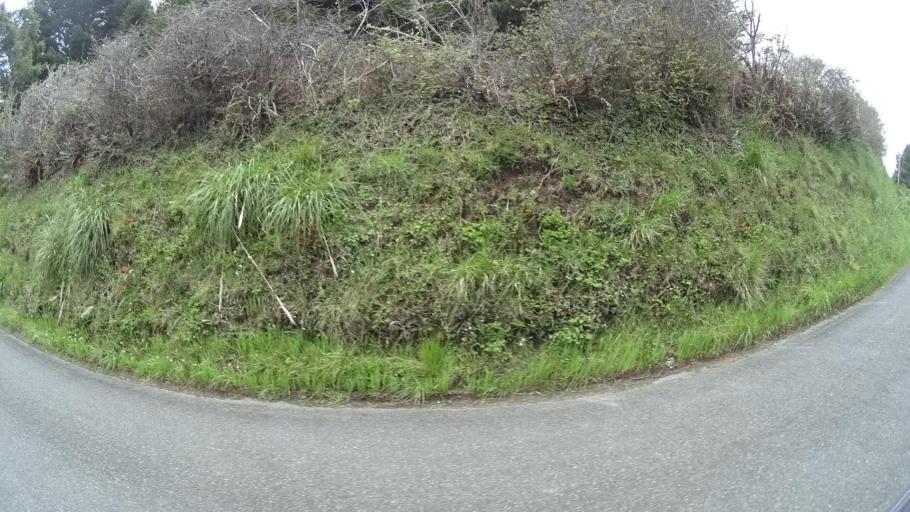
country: US
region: California
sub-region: Humboldt County
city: Humboldt Hill
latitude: 40.6867
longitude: -124.2361
